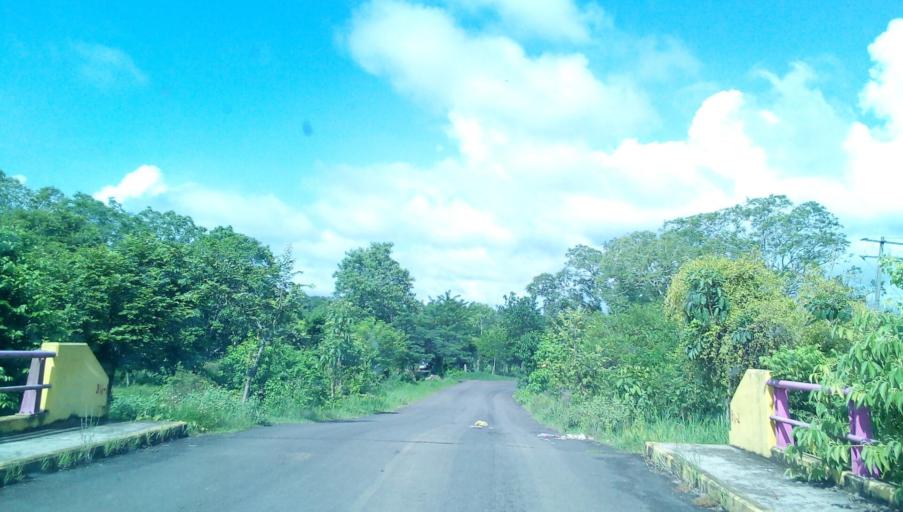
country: MX
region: Veracruz
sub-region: Citlaltepetl
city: Las Sabinas
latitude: 21.3434
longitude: -97.8885
